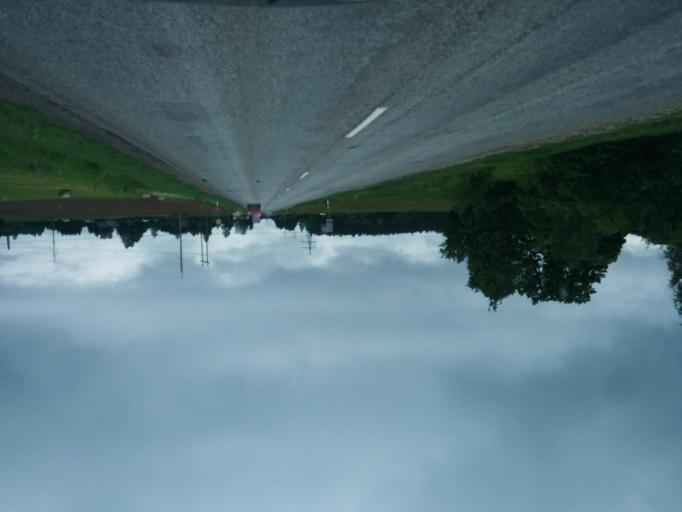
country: LV
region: Beverina
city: Murmuiza
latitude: 57.5088
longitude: 25.4557
